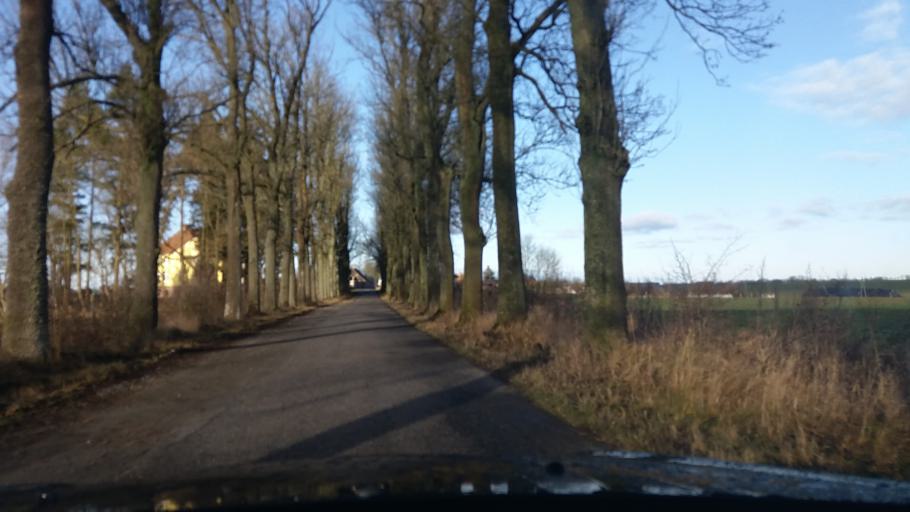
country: PL
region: West Pomeranian Voivodeship
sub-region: Powiat choszczenski
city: Drawno
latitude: 53.1915
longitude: 15.7903
